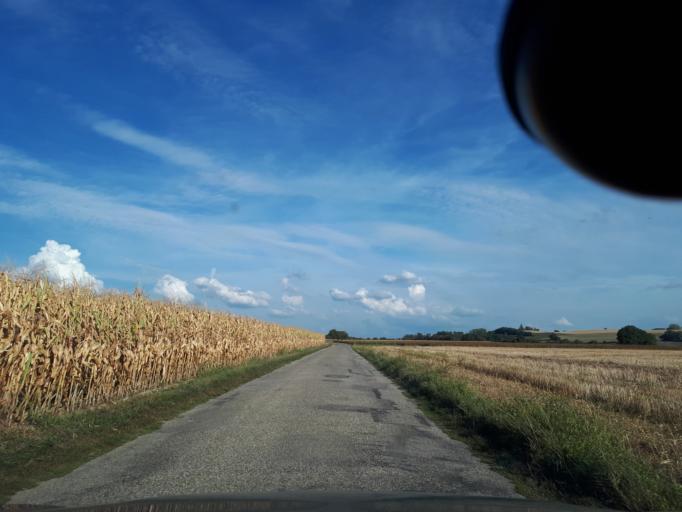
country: FR
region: Rhone-Alpes
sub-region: Departement de l'Isere
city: Chatonnay
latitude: 45.5100
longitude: 5.2102
